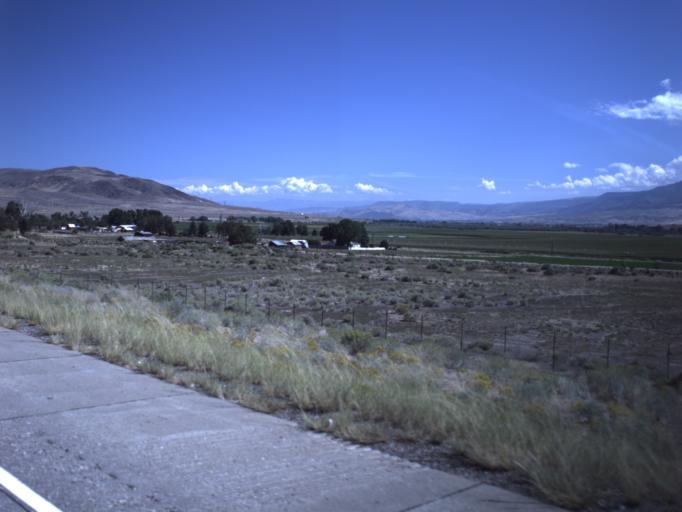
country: US
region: Utah
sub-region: Sevier County
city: Monroe
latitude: 38.6372
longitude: -112.2211
